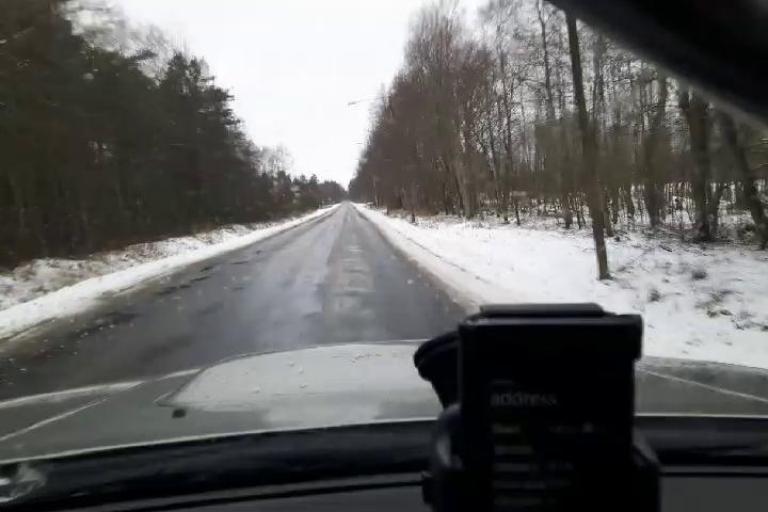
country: EE
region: Harju
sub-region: Harku vald
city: Tabasalu
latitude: 59.4310
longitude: 24.4831
